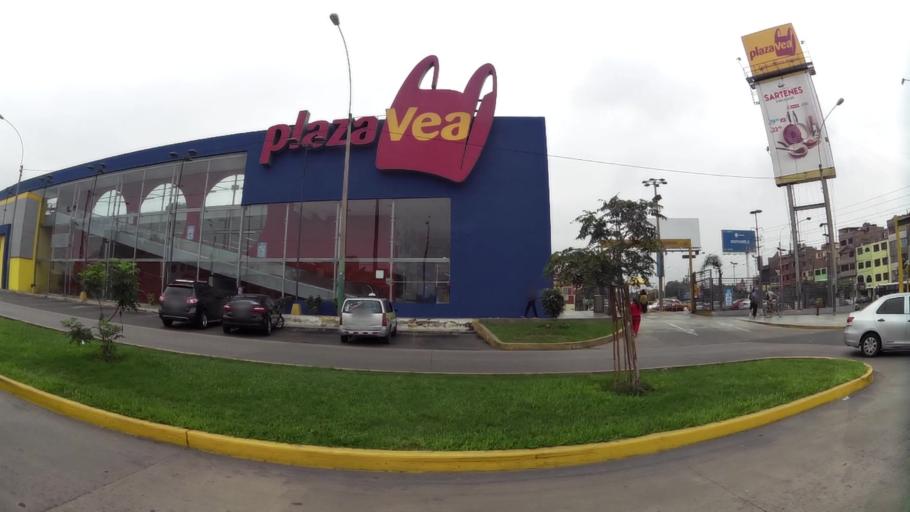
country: PE
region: Lima
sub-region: Lima
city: Surco
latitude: -12.1117
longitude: -77.0074
